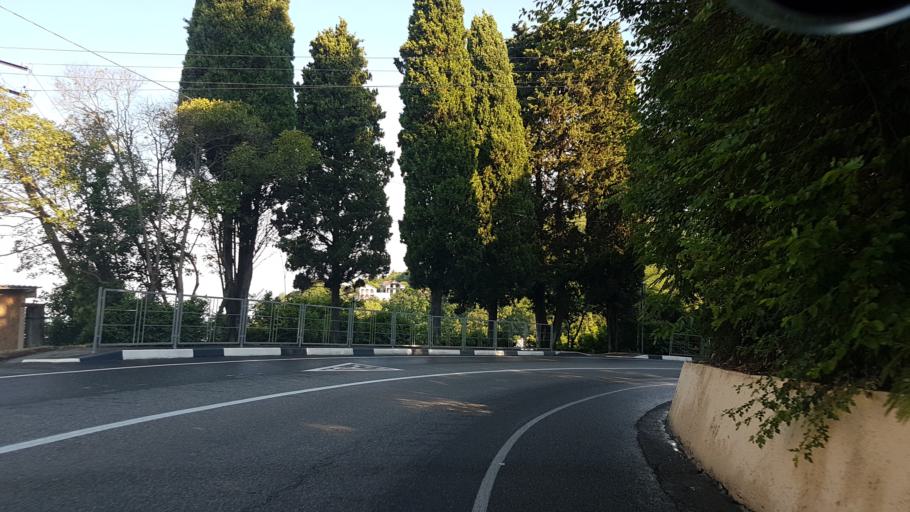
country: RU
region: Krasnodarskiy
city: Vardane
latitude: 43.7984
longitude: 39.4575
